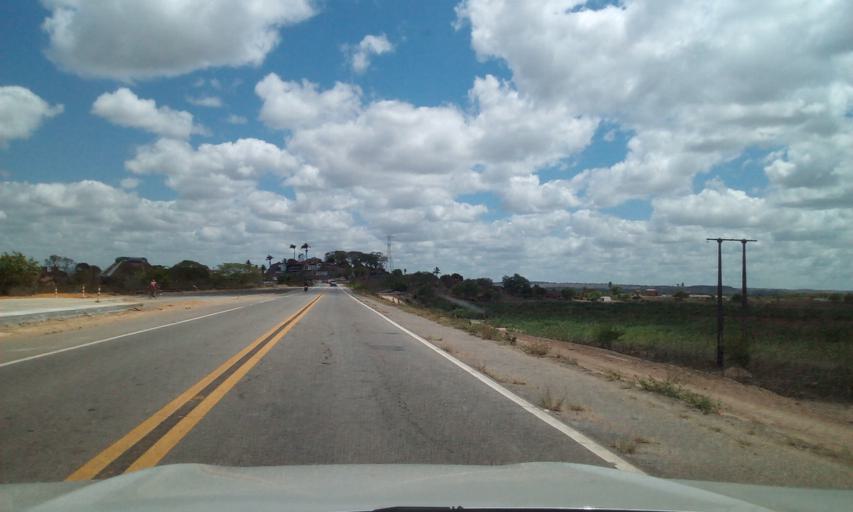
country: BR
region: Sergipe
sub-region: Propria
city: Propria
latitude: -10.2191
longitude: -36.8265
